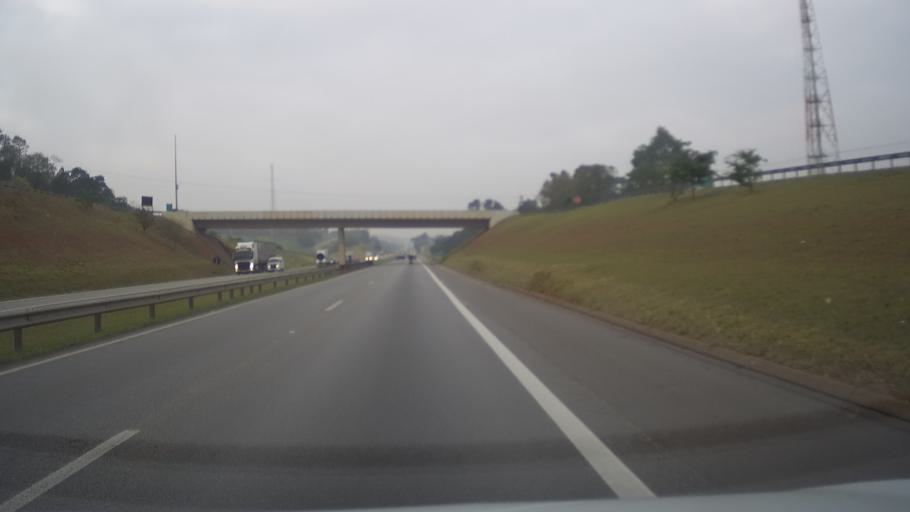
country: BR
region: Sao Paulo
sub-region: Jarinu
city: Jarinu
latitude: -23.0690
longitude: -46.6424
